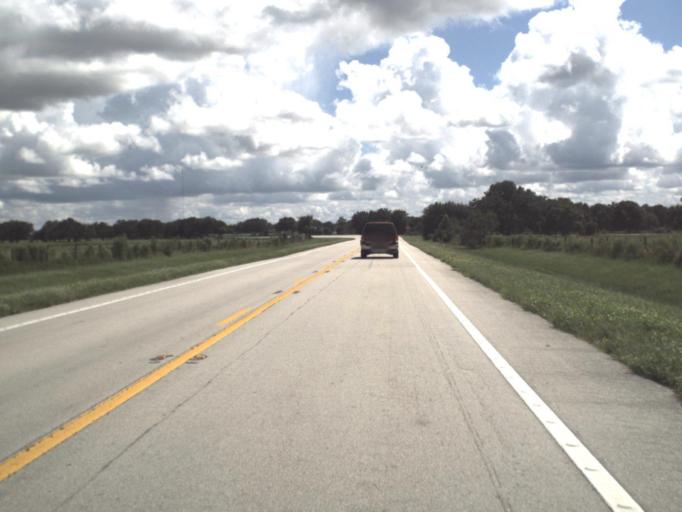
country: US
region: Florida
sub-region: DeSoto County
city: Arcadia
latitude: 27.2368
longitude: -81.9378
